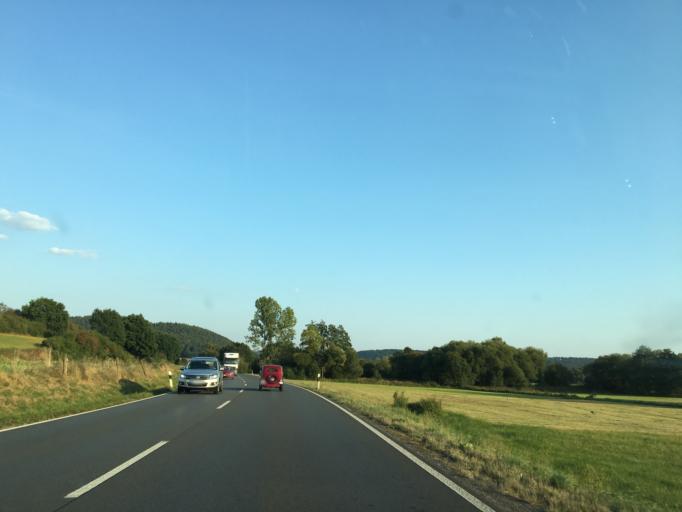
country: DE
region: Hesse
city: Wetter
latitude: 50.8868
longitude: 8.7528
